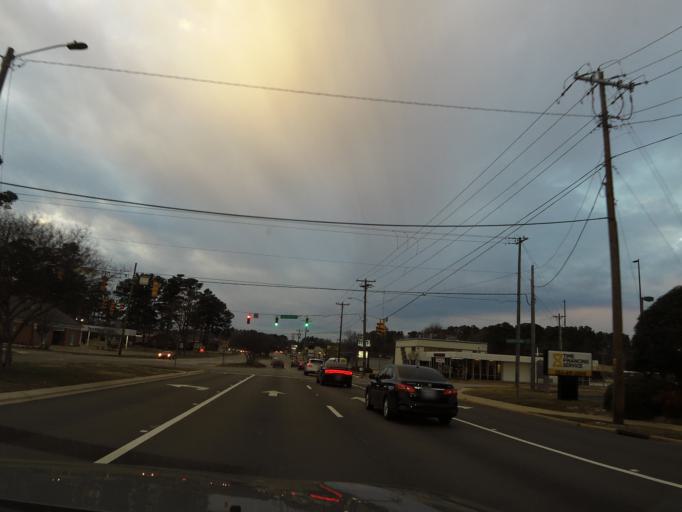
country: US
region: North Carolina
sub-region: Nash County
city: Rocky Mount
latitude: 35.9594
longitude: -77.8254
